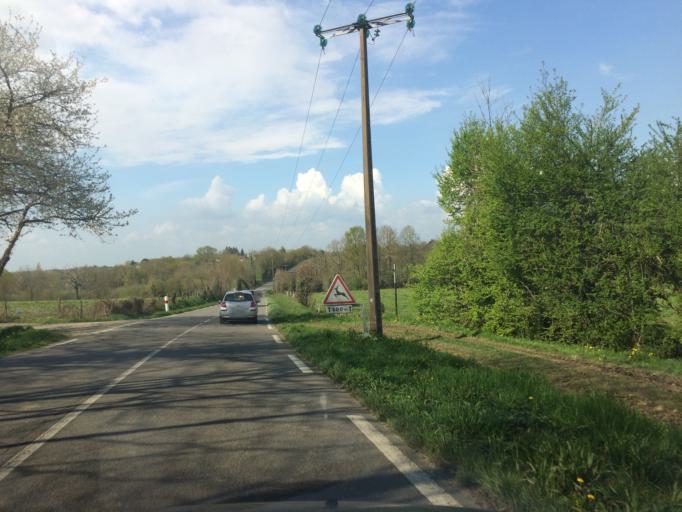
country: FR
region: Pays de la Loire
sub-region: Departement de la Loire-Atlantique
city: Suce-sur-Erdre
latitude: 47.3207
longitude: -1.5108
